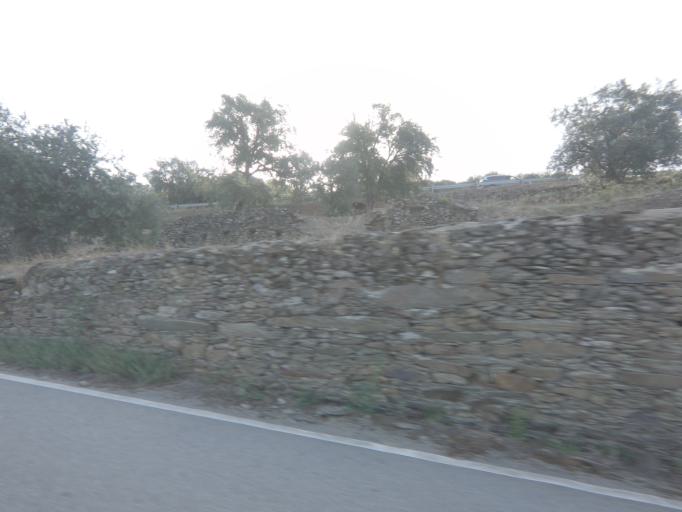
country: PT
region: Vila Real
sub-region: Sabrosa
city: Vilela
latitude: 41.2077
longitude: -7.5343
